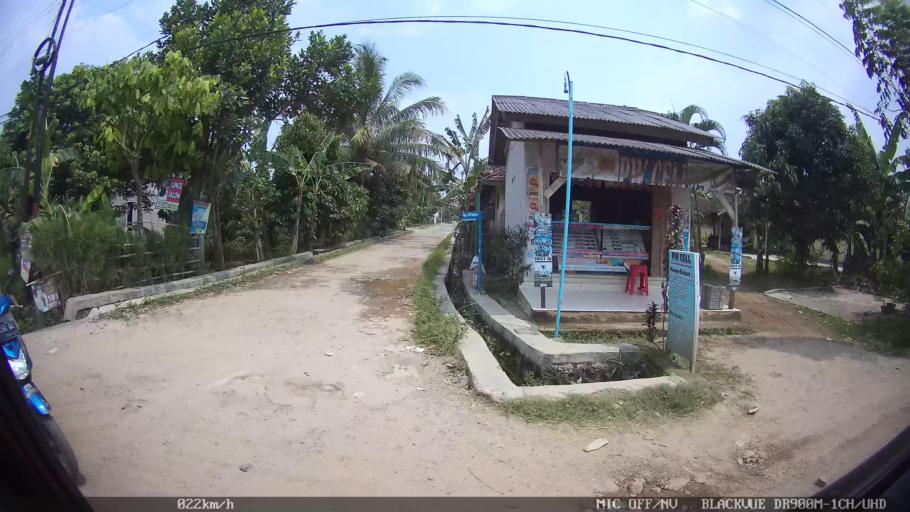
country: ID
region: Lampung
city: Gadingrejo
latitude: -5.3792
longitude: 105.0495
